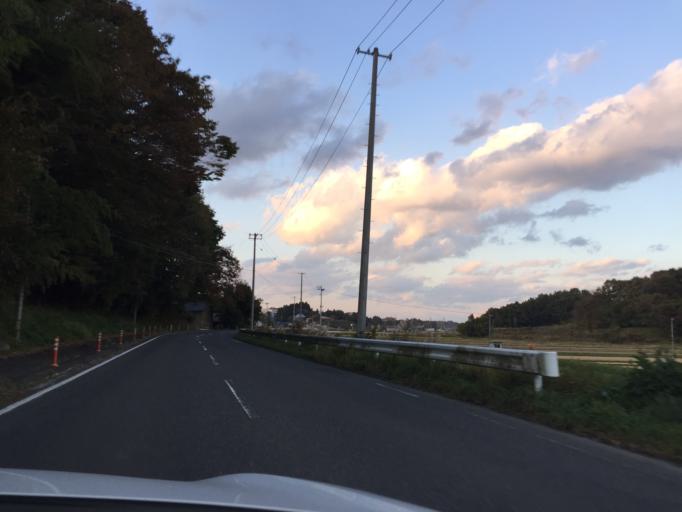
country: JP
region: Fukushima
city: Motomiya
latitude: 37.4867
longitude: 140.4529
